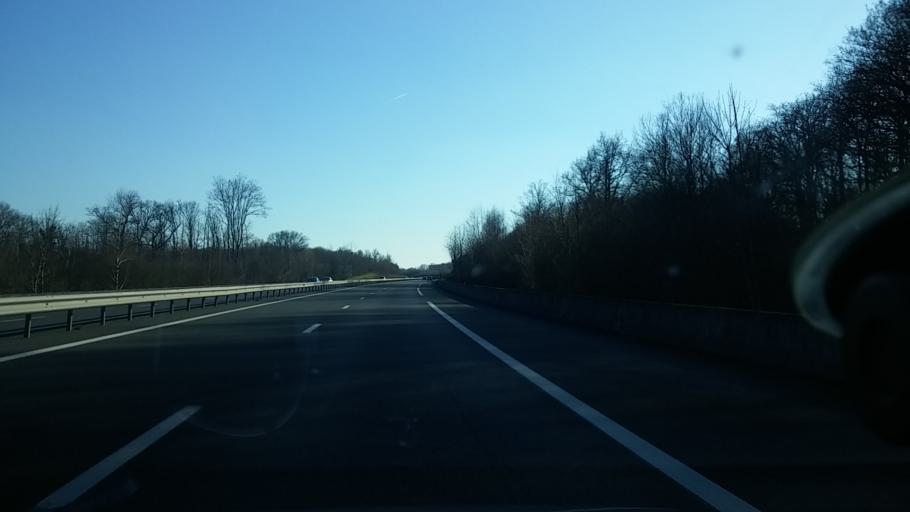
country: FR
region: Centre
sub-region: Departement de l'Indre
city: Chantome
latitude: 46.4037
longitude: 1.4587
